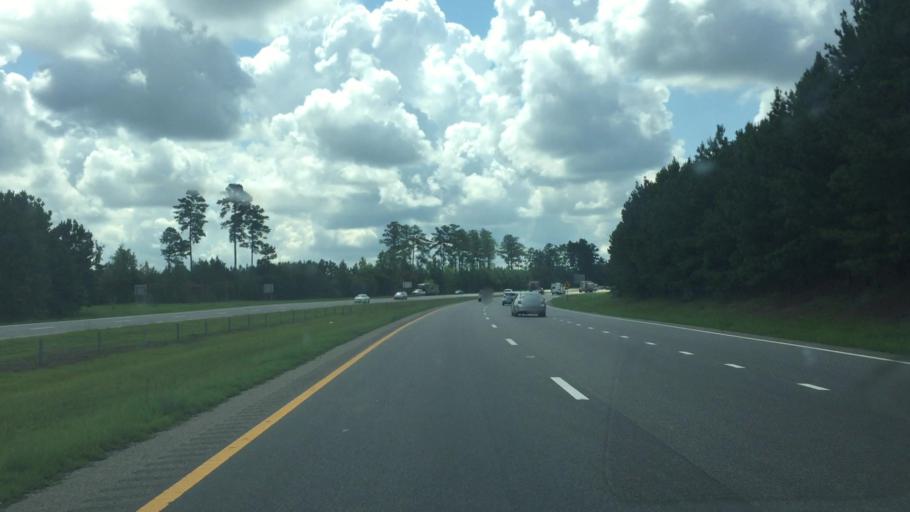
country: US
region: North Carolina
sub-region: Richmond County
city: East Rockingham
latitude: 34.9103
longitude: -79.7918
